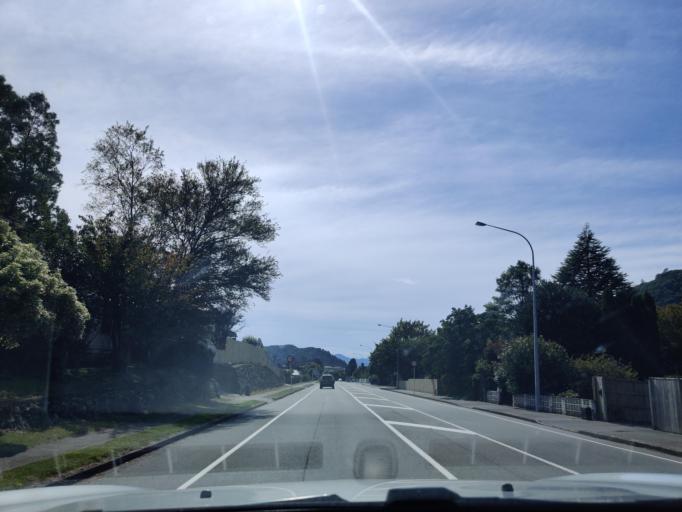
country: NZ
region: Marlborough
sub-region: Marlborough District
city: Picton
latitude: -41.2993
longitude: 173.9986
